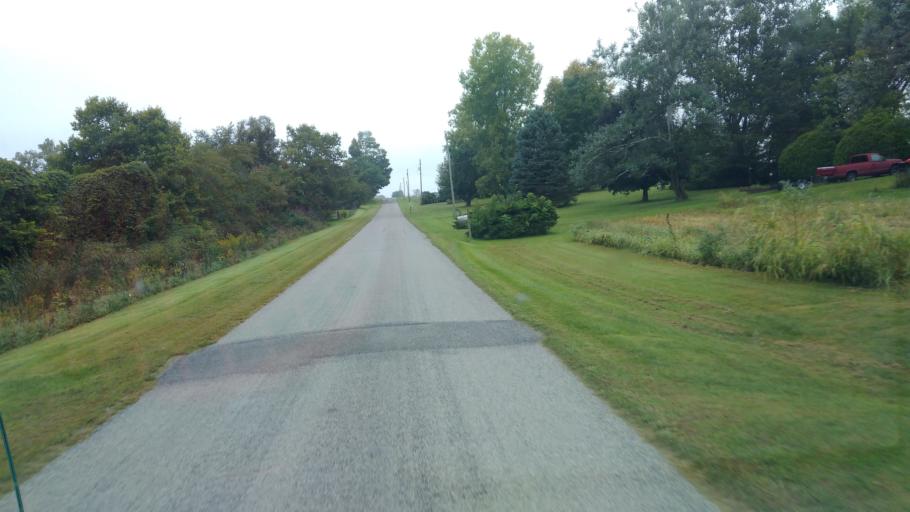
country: US
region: Ohio
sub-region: Union County
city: Richwood
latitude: 40.5027
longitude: -83.3342
